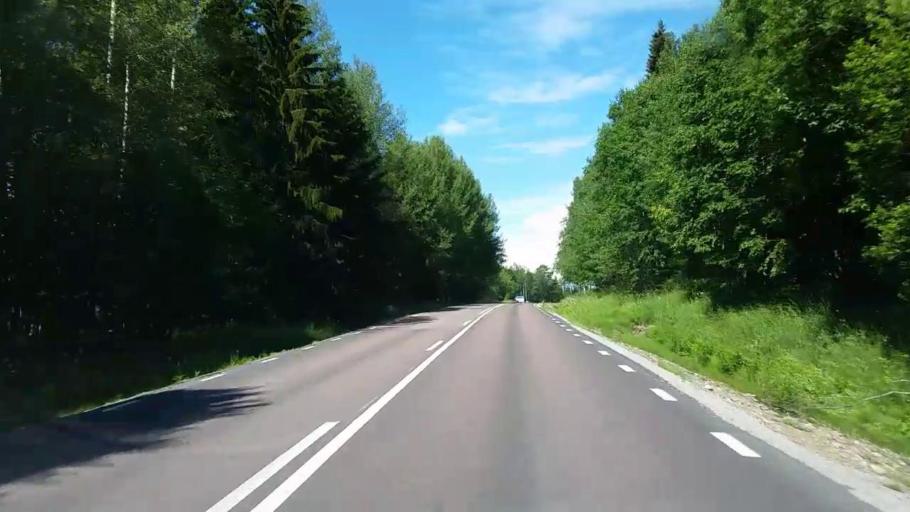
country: SE
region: Dalarna
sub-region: Rattviks Kommun
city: Raettvik
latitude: 61.0163
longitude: 15.2130
